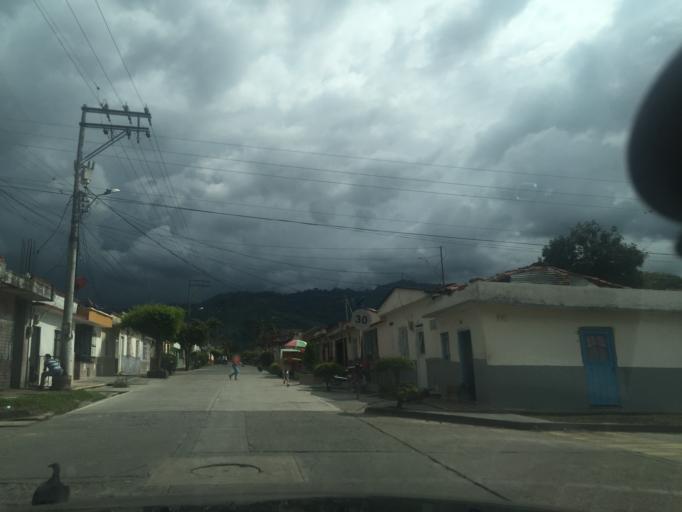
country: CO
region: Valle del Cauca
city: Caicedonia
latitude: 4.3398
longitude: -75.8317
